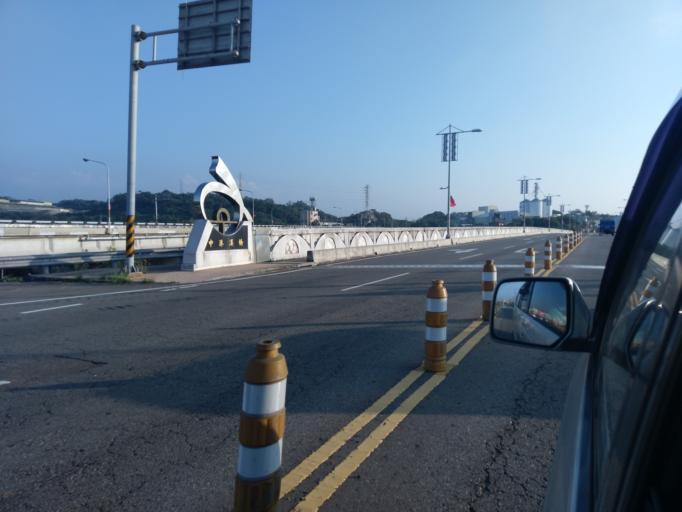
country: TW
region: Taiwan
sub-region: Miaoli
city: Miaoli
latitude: 24.6688
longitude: 120.8819
